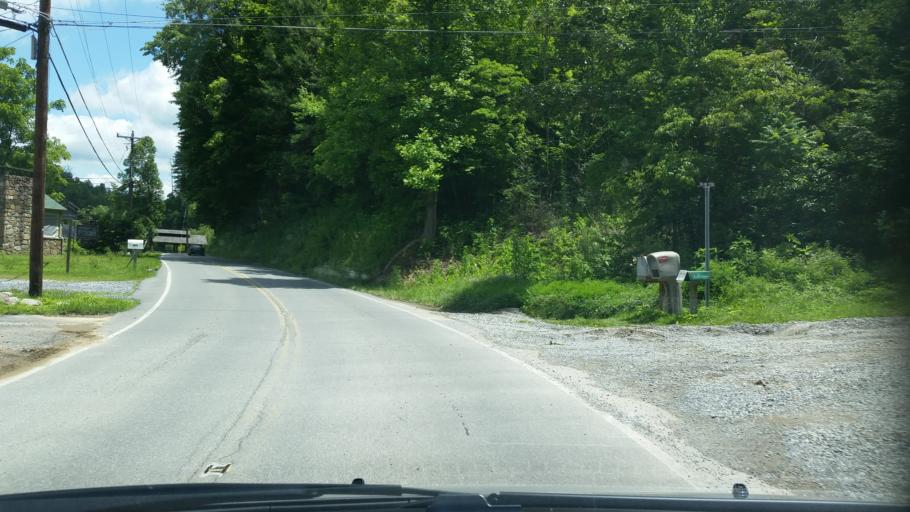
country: US
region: Tennessee
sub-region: Sevier County
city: Gatlinburg
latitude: 35.7462
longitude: -83.4507
